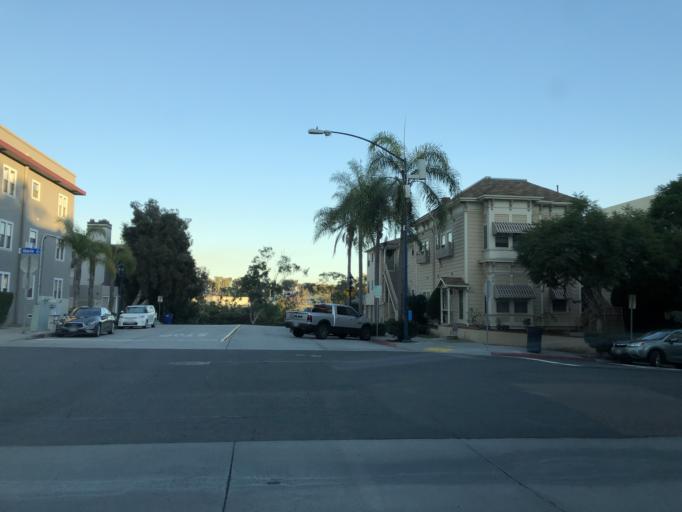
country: US
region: California
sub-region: San Diego County
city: San Diego
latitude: 32.7220
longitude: -117.1568
